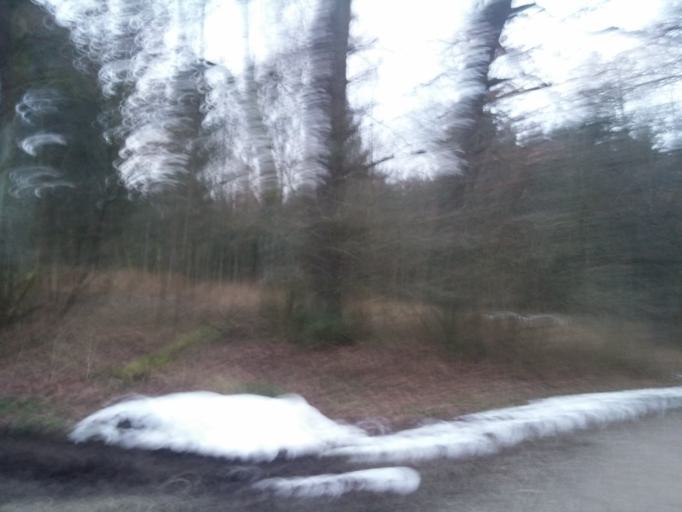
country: DE
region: Bavaria
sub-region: Upper Bavaria
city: Putzbrunn
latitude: 48.0645
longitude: 11.7199
